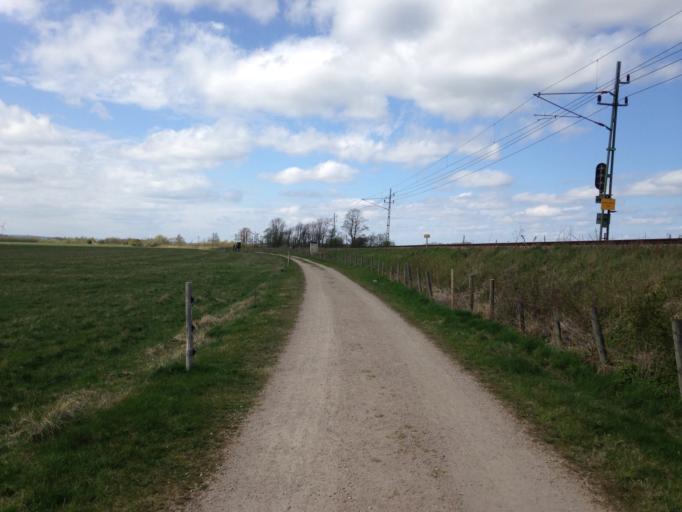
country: SE
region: Skane
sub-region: Kristianstads Kommun
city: Kristianstad
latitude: 56.0406
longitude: 14.1404
